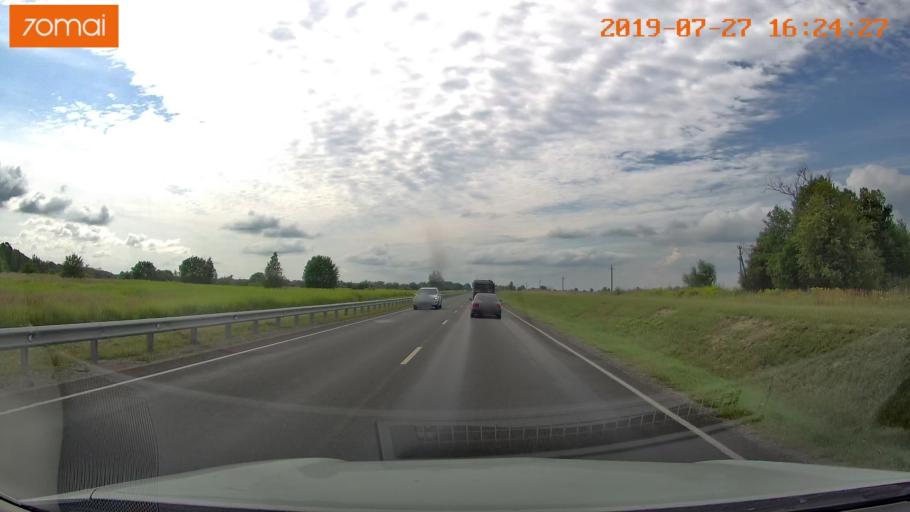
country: RU
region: Kaliningrad
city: Zheleznodorozhnyy
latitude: 54.6342
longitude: 21.4523
